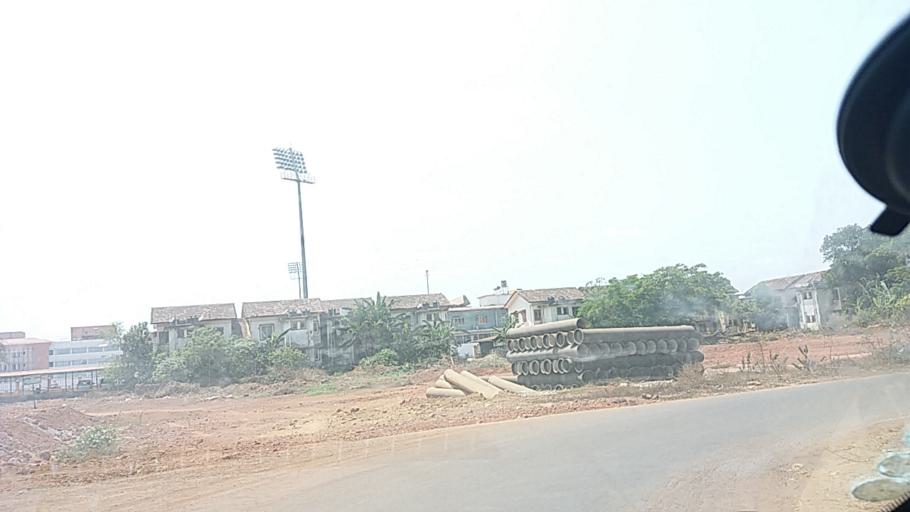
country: IN
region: Goa
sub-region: North Goa
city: Serula
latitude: 15.5246
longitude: 73.8314
